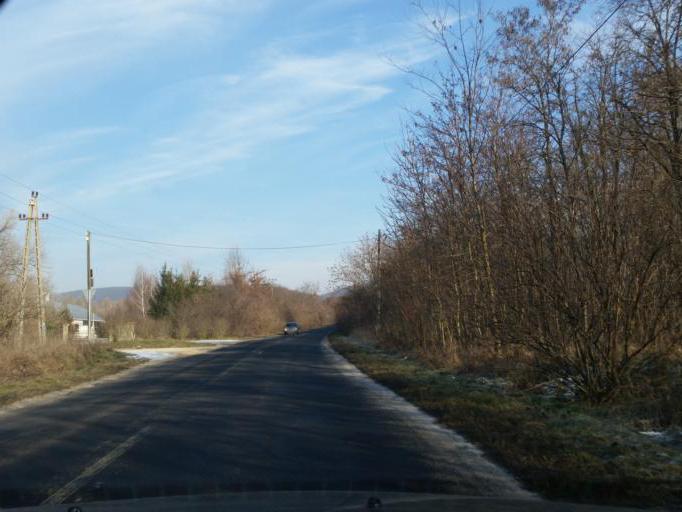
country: HU
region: Pest
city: Paty
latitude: 47.5274
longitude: 18.8366
